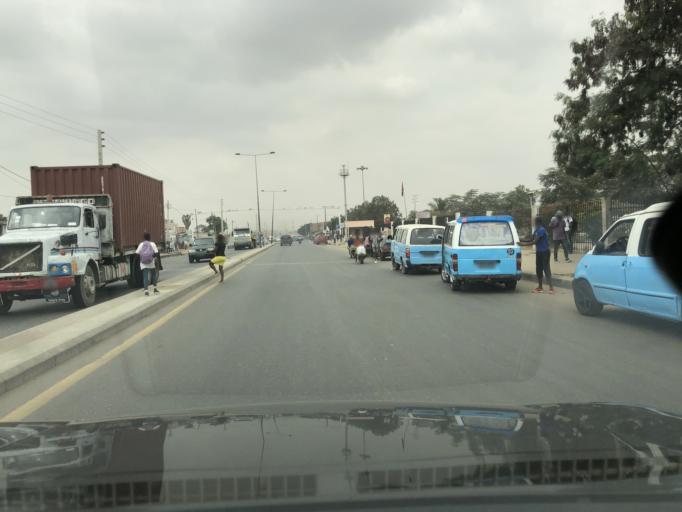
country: AO
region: Luanda
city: Luanda
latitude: -8.8289
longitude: 13.2828
